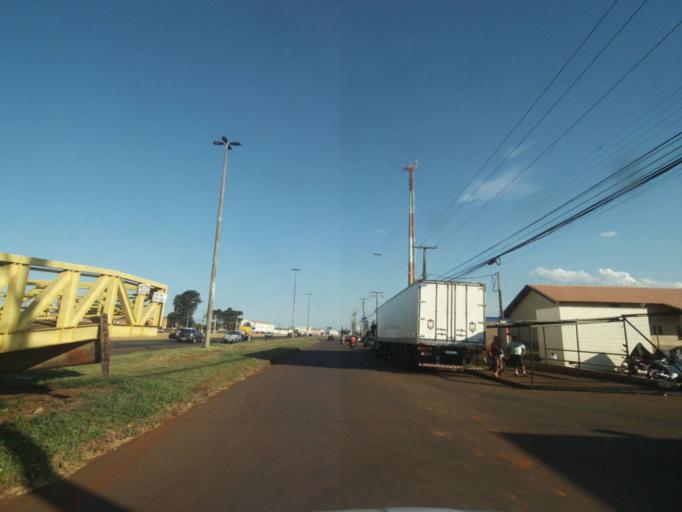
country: BR
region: Parana
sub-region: Cambe
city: Cambe
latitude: -23.2991
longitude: -51.2293
